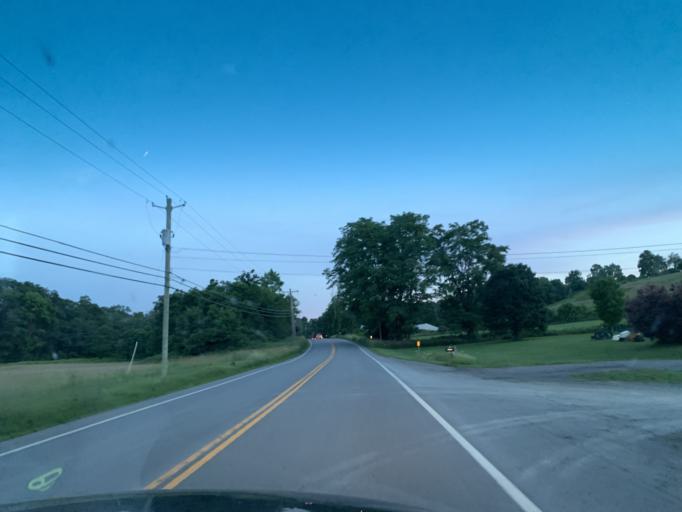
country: US
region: New York
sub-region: Chenango County
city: New Berlin
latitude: 42.6394
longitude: -75.3313
